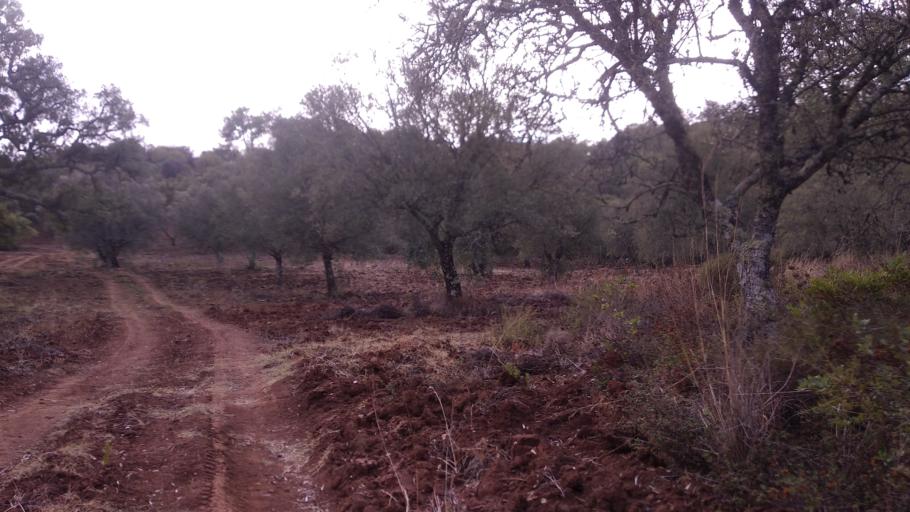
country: PT
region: Faro
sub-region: Sao Bras de Alportel
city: Sao Bras de Alportel
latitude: 37.1616
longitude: -7.9075
